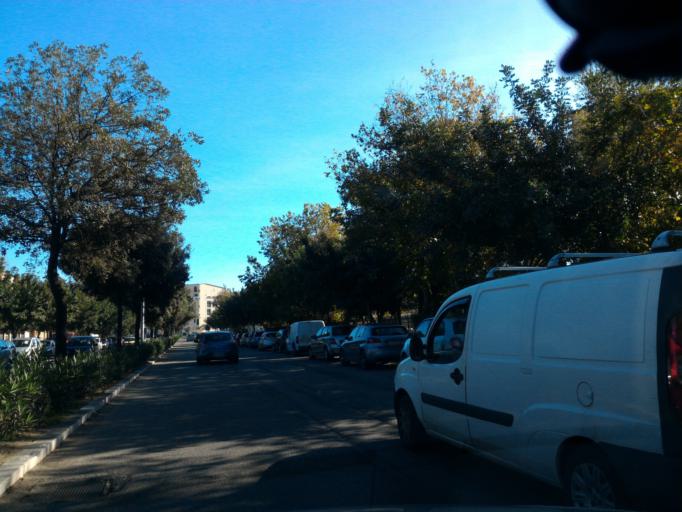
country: IT
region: Calabria
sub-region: Provincia di Crotone
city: Crotone
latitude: 39.0804
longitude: 17.1202
